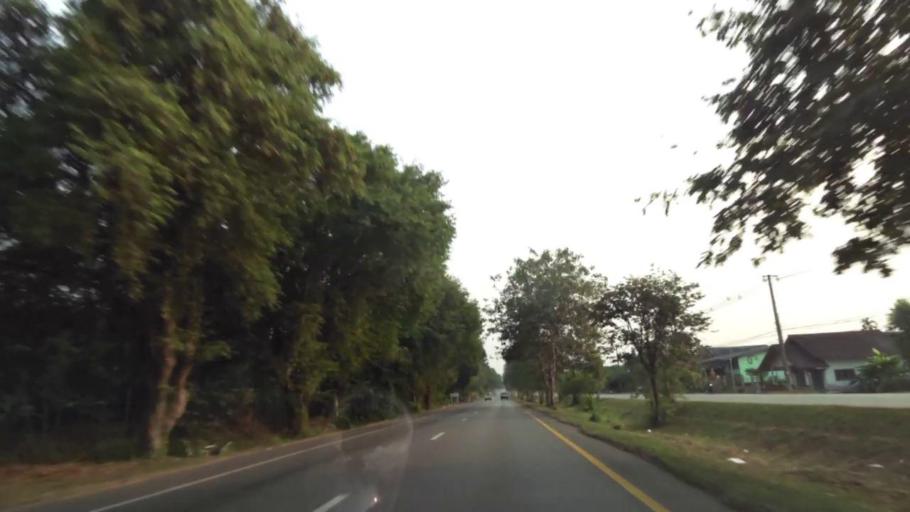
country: TH
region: Chanthaburi
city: Khlung
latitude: 12.4938
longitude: 102.1731
